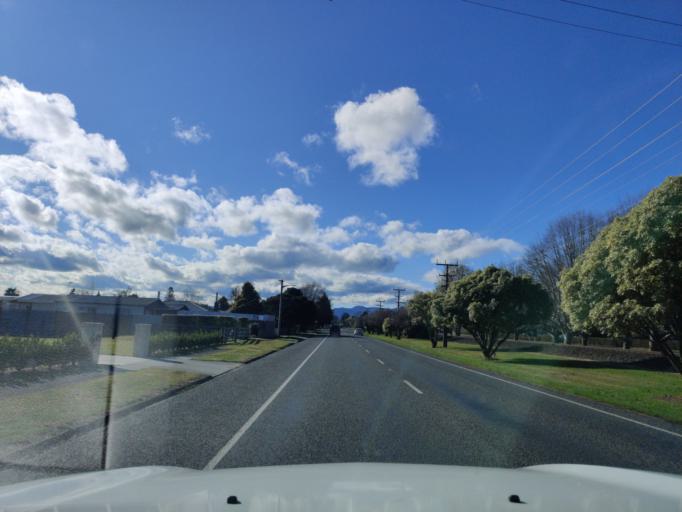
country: NZ
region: Waikato
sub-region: Matamata-Piako District
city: Matamata
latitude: -37.8288
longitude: 175.7685
